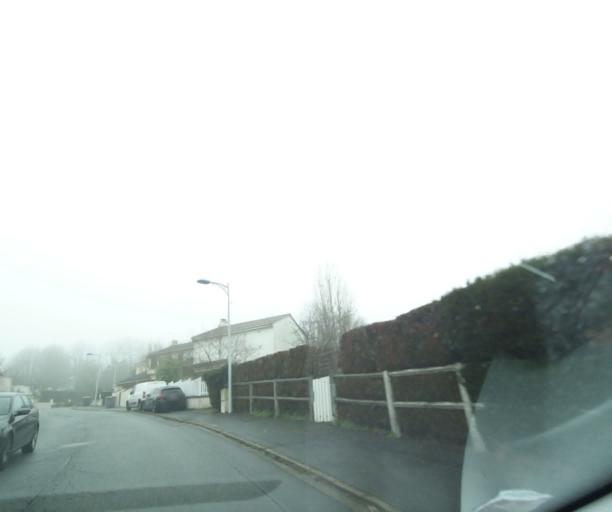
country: FR
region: Ile-de-France
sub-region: Departement de Seine-et-Marne
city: Dammartin-en-Goele
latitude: 49.0566
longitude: 2.6945
